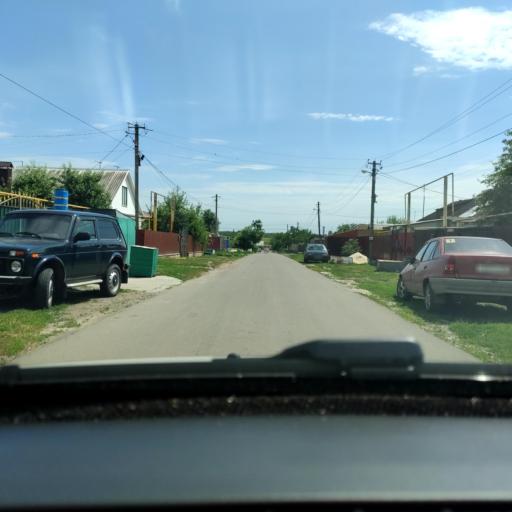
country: RU
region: Voronezj
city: Maslovka
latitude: 51.5043
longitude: 39.2976
